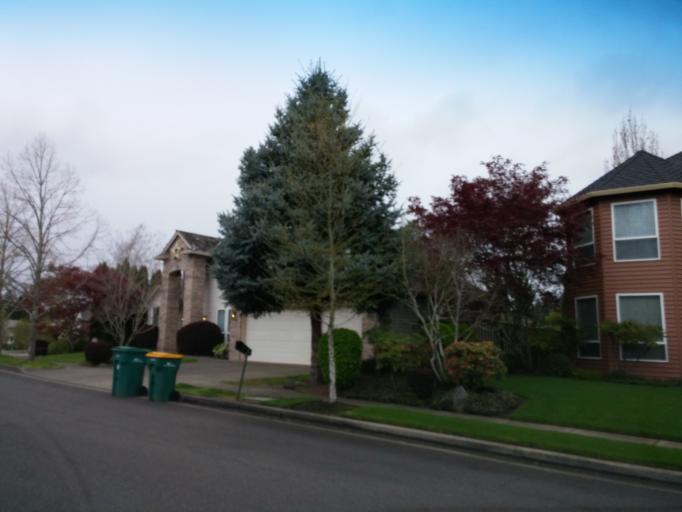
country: US
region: Oregon
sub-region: Washington County
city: Oak Hills
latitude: 45.5251
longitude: -122.8480
